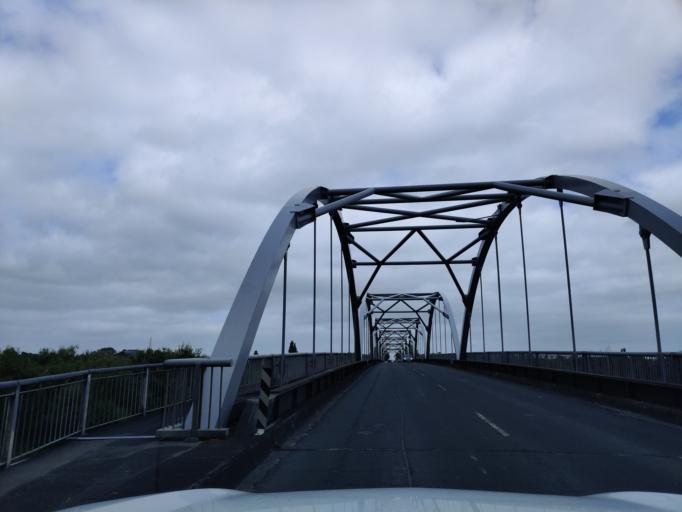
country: NZ
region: Waikato
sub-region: Waikato District
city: Ngaruawahia
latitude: -37.5665
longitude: 175.1567
